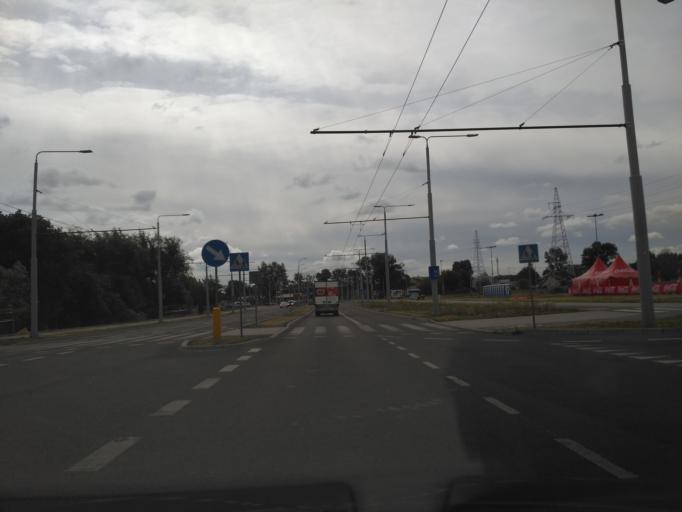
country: PL
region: Lublin Voivodeship
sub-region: Powiat lubelski
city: Lublin
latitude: 51.2338
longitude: 22.5589
